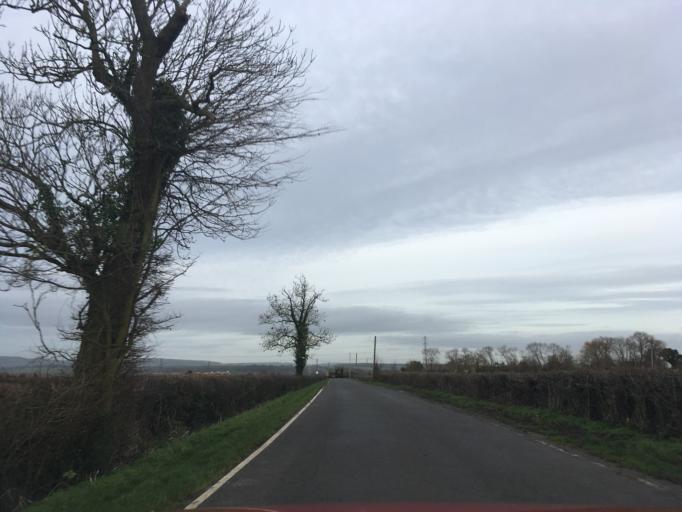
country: GB
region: Wales
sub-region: Newport
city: Redwick
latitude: 51.5589
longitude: -2.8335
